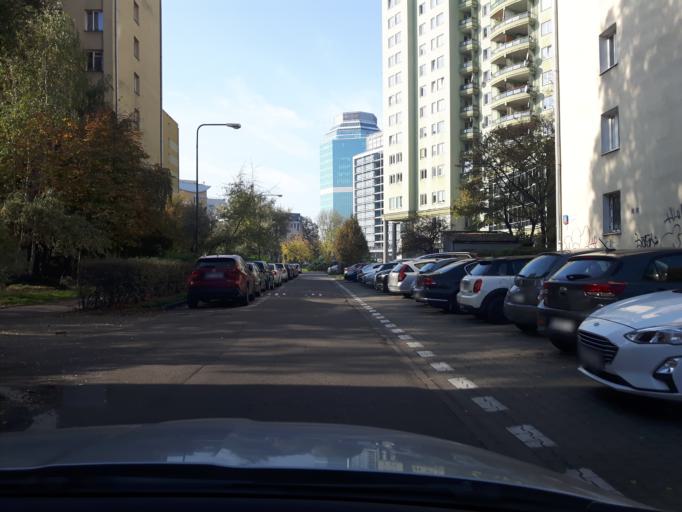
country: PL
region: Masovian Voivodeship
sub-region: Warszawa
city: Ochota
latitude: 52.2206
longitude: 20.9768
